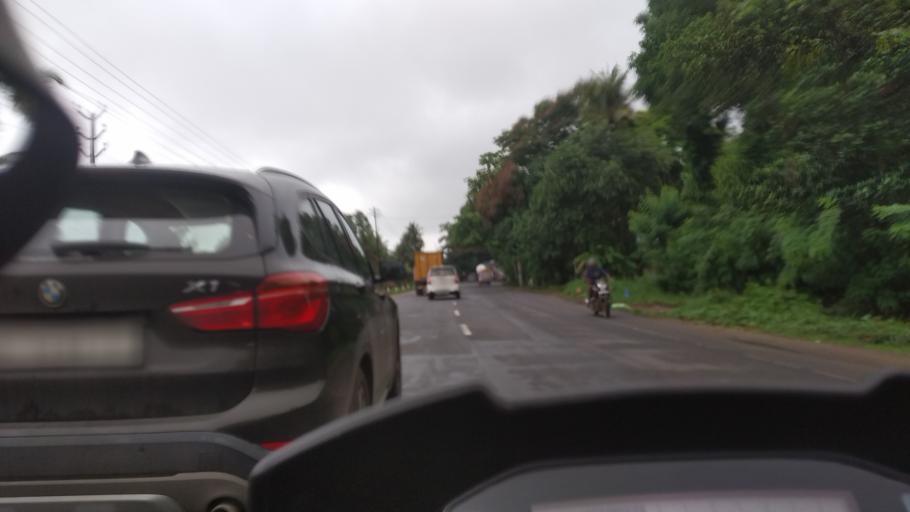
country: IN
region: Kerala
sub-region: Alappuzha
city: Mavelikara
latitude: 9.3161
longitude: 76.4148
